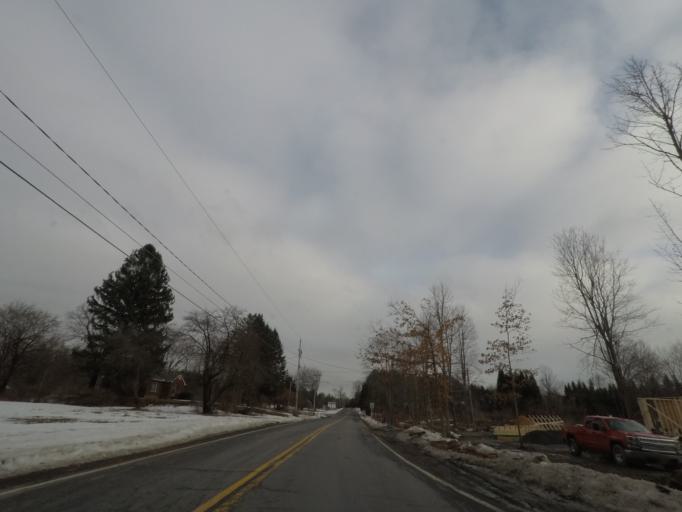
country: US
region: New York
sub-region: Schenectady County
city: Rotterdam
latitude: 42.7293
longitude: -73.9550
